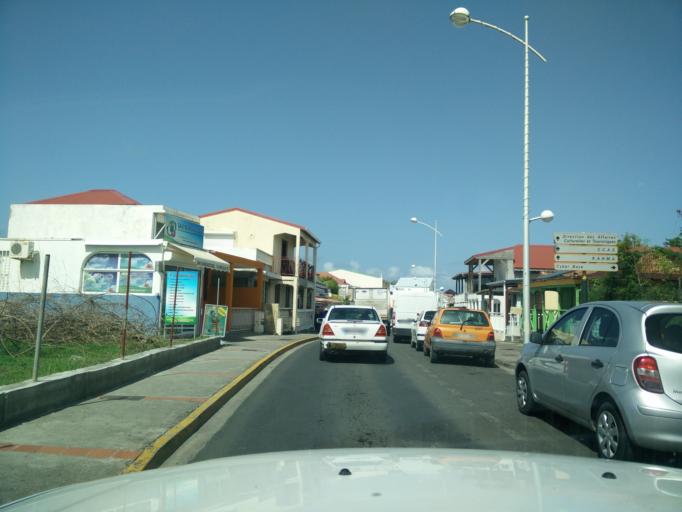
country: GP
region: Guadeloupe
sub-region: Guadeloupe
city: Le Gosier
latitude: 16.2061
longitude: -61.4874
